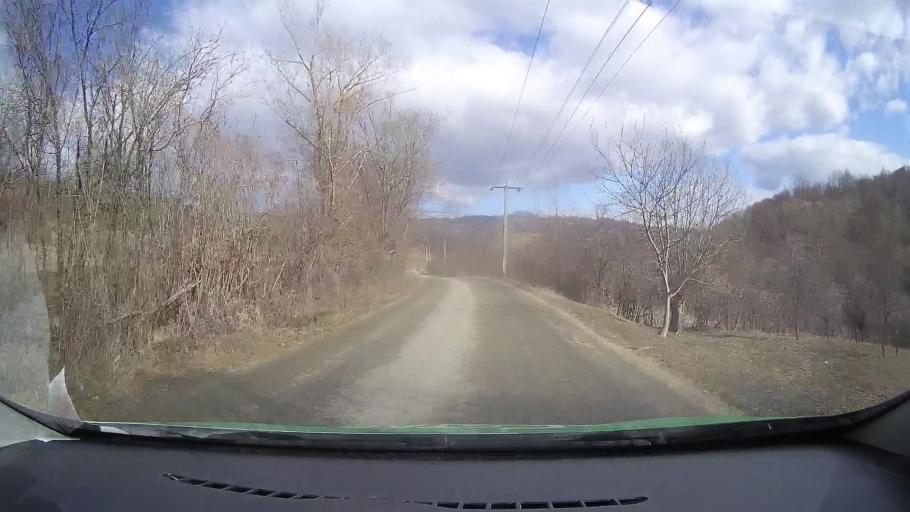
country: RO
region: Dambovita
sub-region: Comuna Motaeni
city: Motaeni
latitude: 45.1111
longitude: 25.4421
